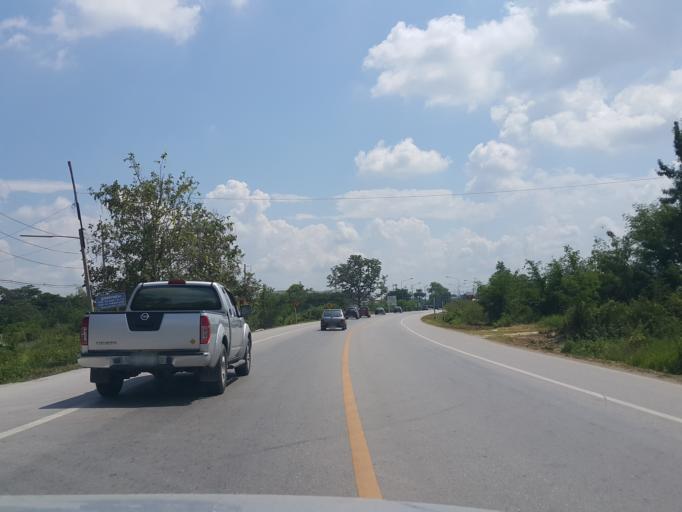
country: TH
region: Chiang Mai
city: San Sai
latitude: 18.8290
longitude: 99.0457
